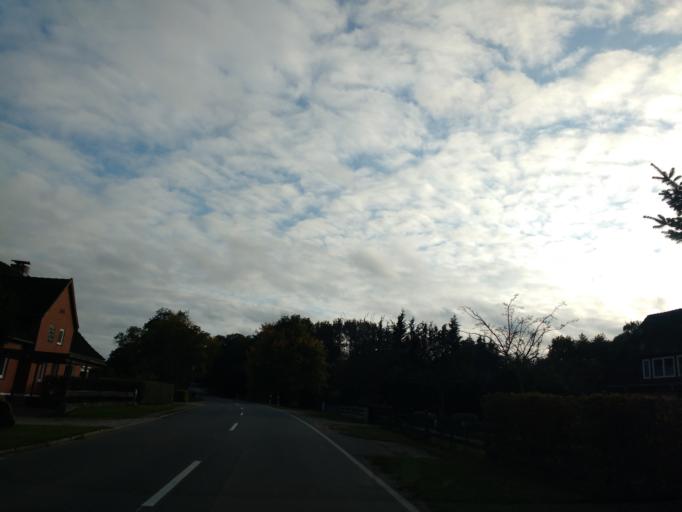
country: DE
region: Schleswig-Holstein
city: Schonwalde am Bungsberg
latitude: 54.2165
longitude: 10.7377
